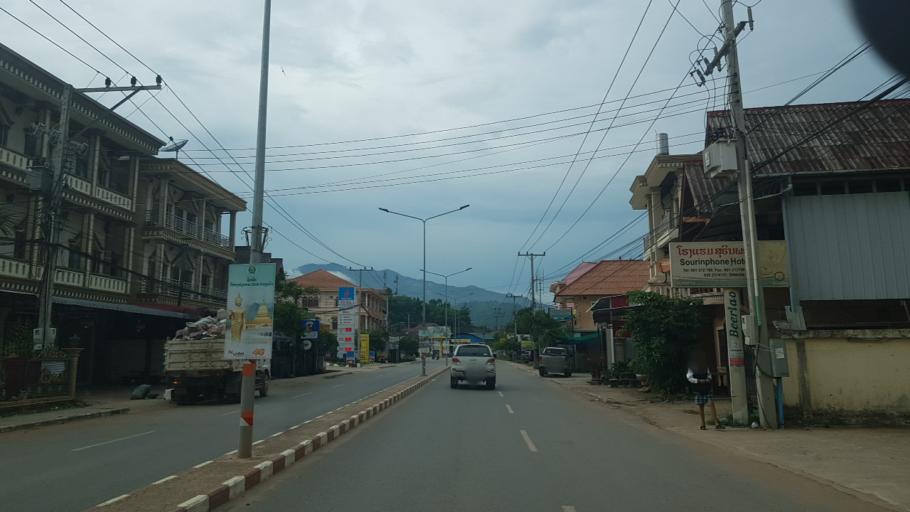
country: LA
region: Oudomxai
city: Muang Xay
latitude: 20.6838
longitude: 101.9872
